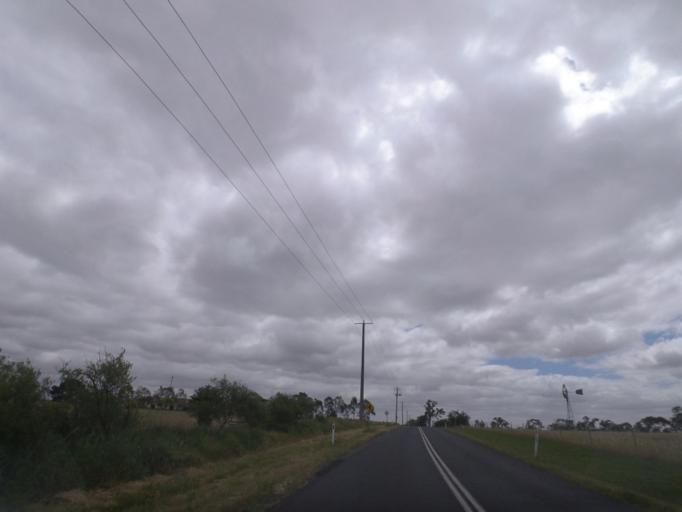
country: AU
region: Victoria
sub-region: Whittlesea
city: Whittlesea
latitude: -37.1875
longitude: 145.0380
